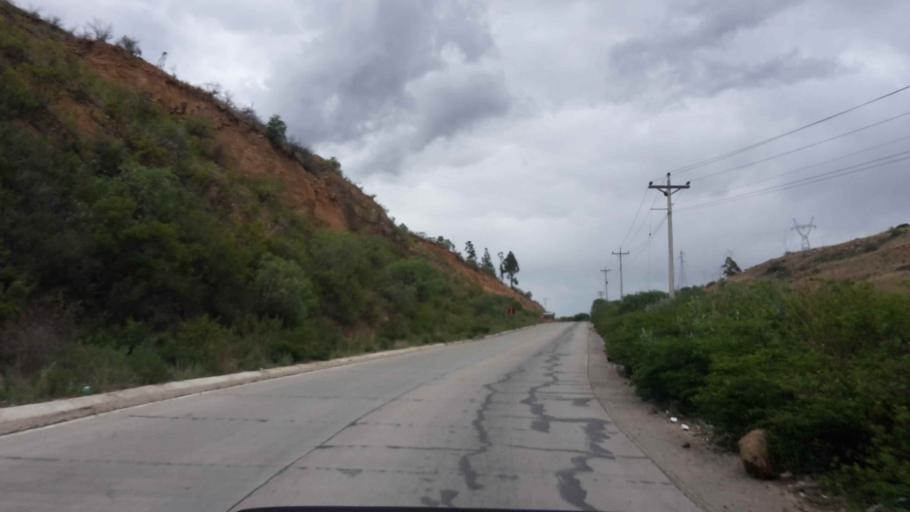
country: BO
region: Cochabamba
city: Cochabamba
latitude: -17.5303
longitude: -66.1968
